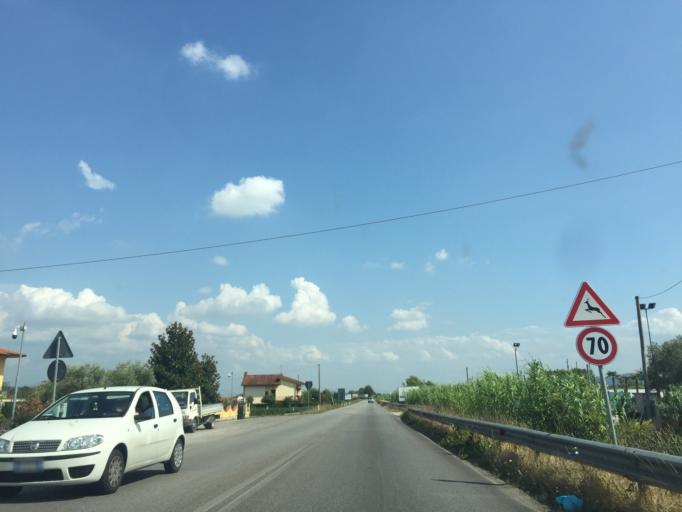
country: IT
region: Tuscany
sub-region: Provincia di Pistoia
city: Cantagrillo-Casalguidi
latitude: 43.8819
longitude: 10.9190
